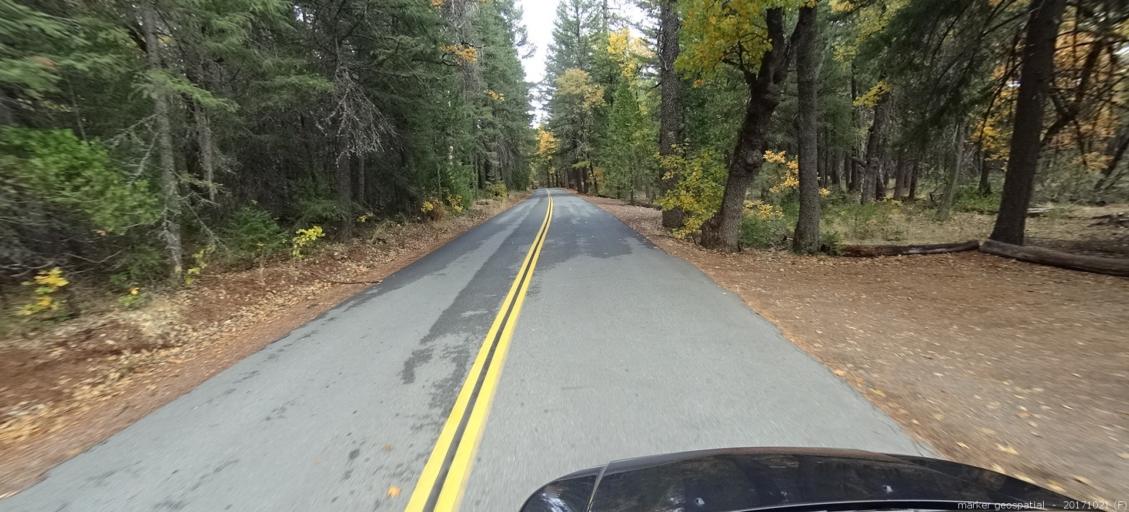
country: US
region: California
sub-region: Shasta County
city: Burney
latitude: 41.0108
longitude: -121.6539
